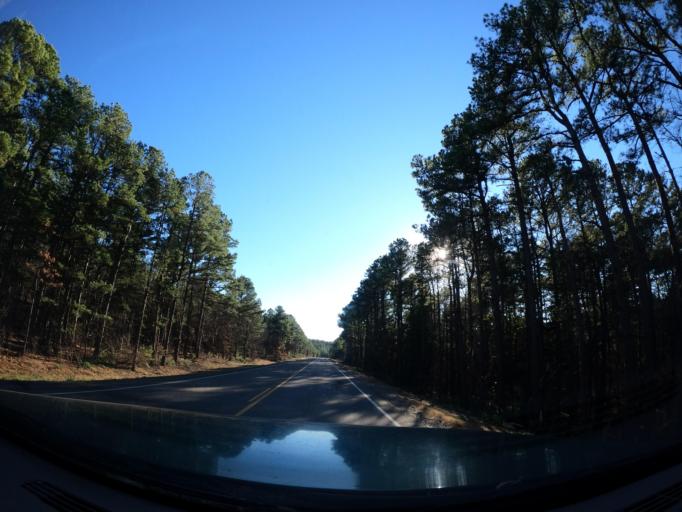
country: US
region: Oklahoma
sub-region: Latimer County
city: Wilburton
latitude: 34.9899
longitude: -95.3517
